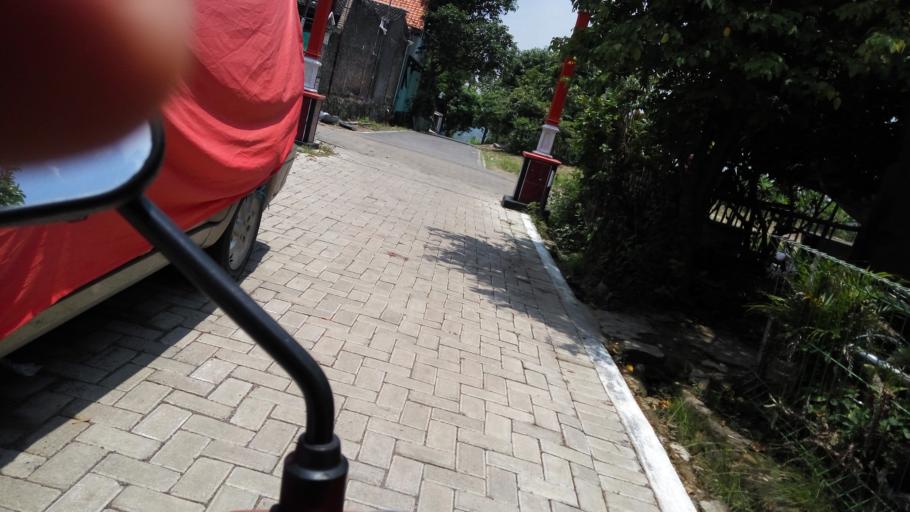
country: ID
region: Central Java
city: Mranggen
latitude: -7.0462
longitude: 110.4756
